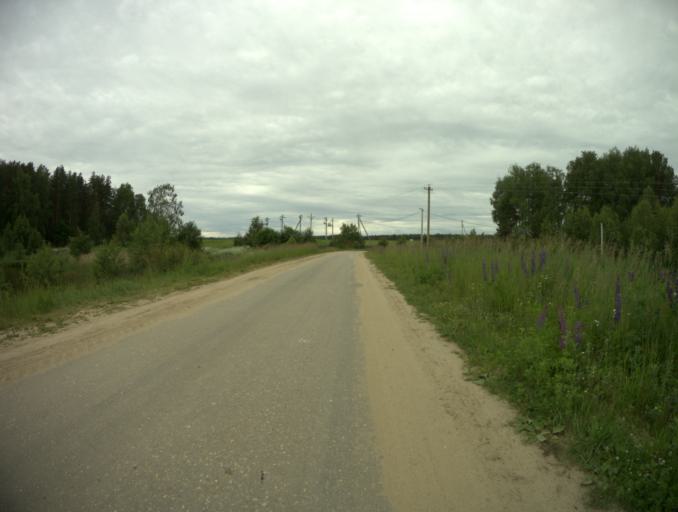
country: RU
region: Vladimir
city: Kommunar
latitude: 56.0485
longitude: 40.4788
